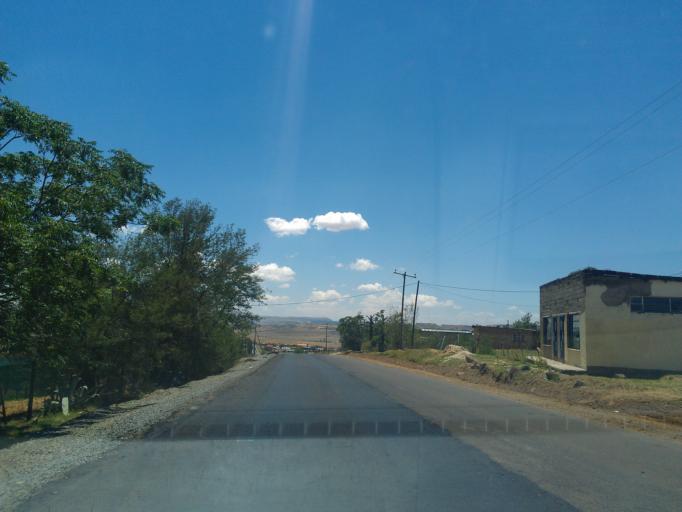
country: LS
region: Berea
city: Teyateyaneng
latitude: -29.1460
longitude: 27.7587
